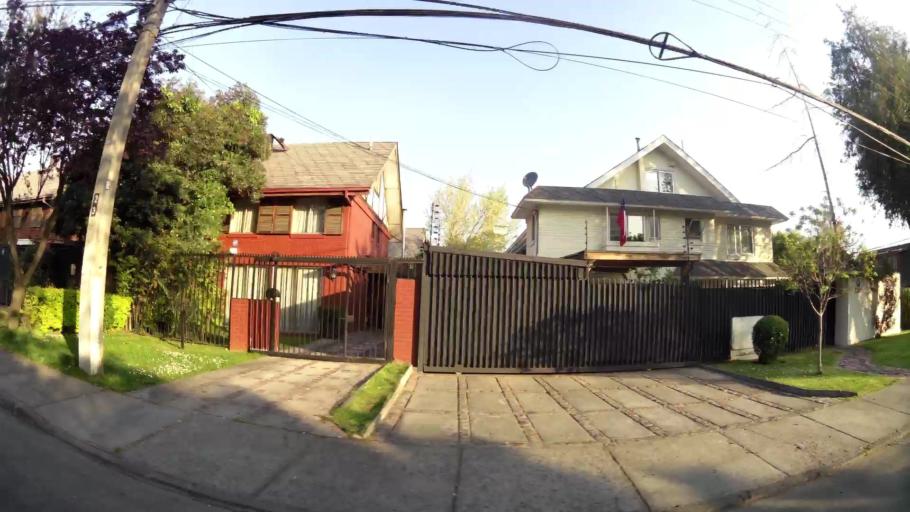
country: CL
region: Santiago Metropolitan
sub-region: Provincia de Santiago
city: Villa Presidente Frei, Nunoa, Santiago, Chile
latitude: -33.3926
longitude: -70.5488
